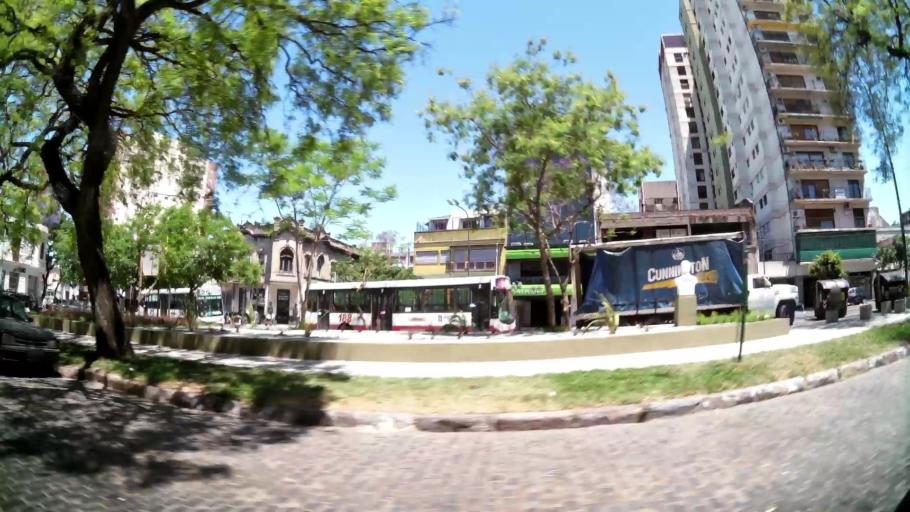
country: AR
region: Buenos Aires F.D.
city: Buenos Aires
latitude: -34.6351
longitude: -58.3900
